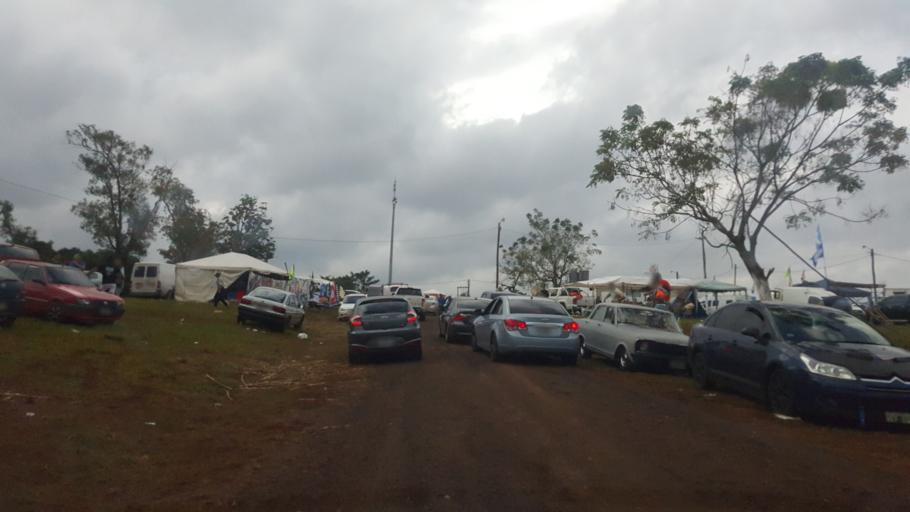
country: AR
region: Misiones
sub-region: Departamento de Capital
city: Posadas
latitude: -27.4361
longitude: -55.9283
